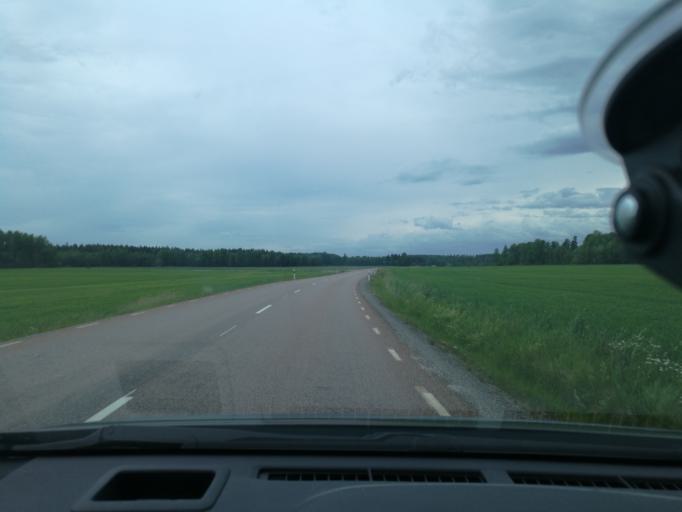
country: SE
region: Vaestmanland
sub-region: Vasteras
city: Skultuna
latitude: 59.7346
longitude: 16.4134
